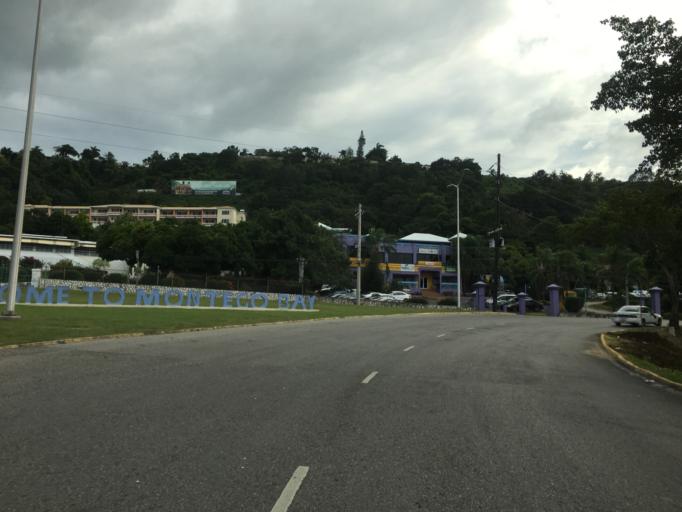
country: JM
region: Saint James
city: Montego Bay
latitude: 18.4950
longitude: -77.9168
